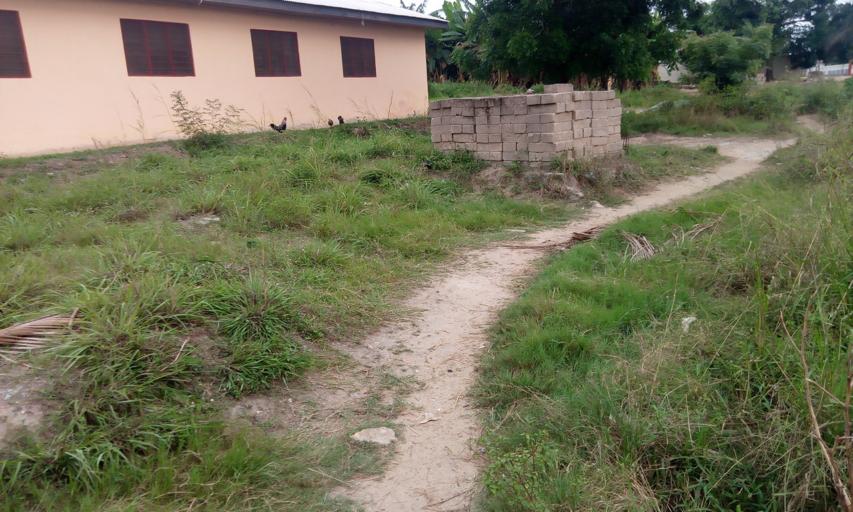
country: GH
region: Central
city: Winneba
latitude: 5.3594
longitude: -0.6290
